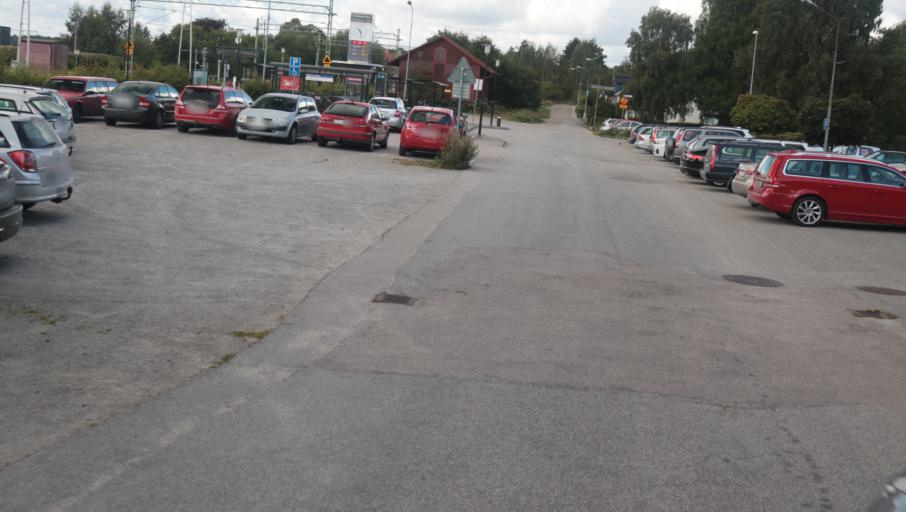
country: SE
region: Blekinge
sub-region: Karlshamns Kommun
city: Morrum
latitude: 56.1870
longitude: 14.7453
